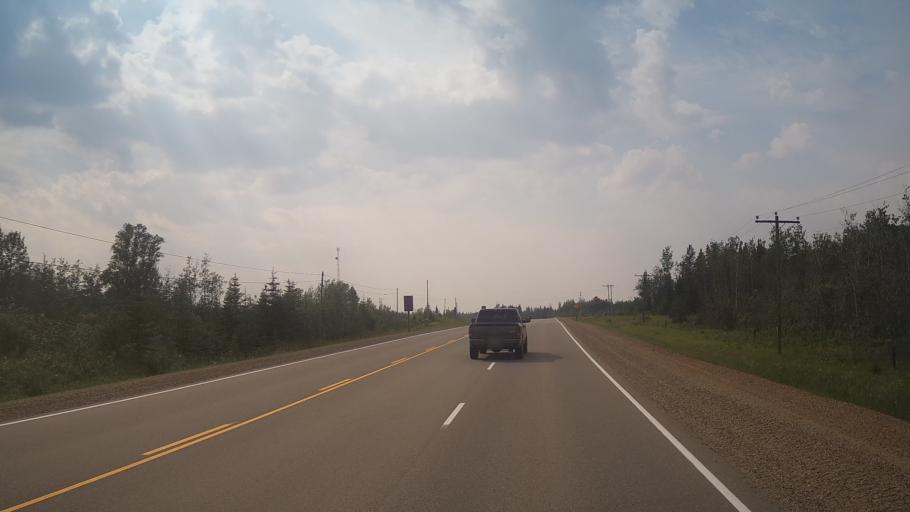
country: CA
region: Ontario
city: Kapuskasing
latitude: 49.4577
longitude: -82.5740
